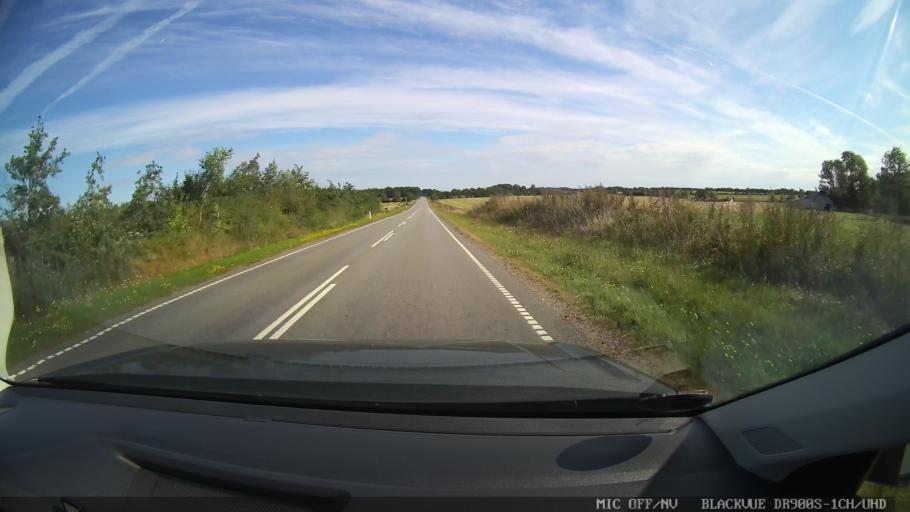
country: DK
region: North Denmark
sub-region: Mariagerfjord Kommune
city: Hadsund
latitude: 56.7811
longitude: 10.0128
